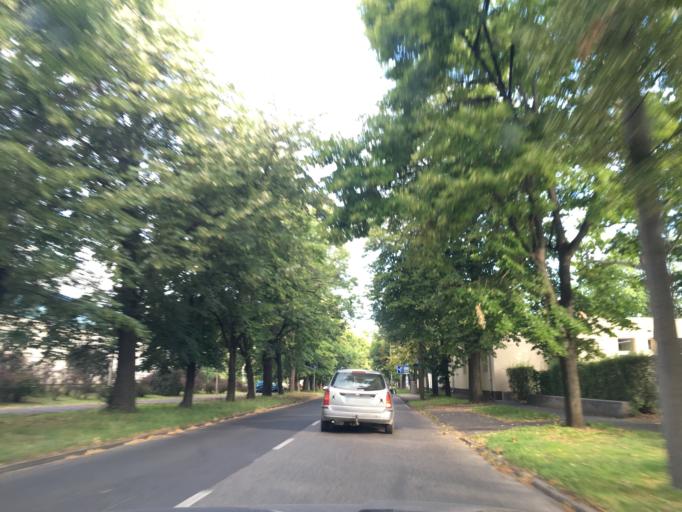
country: HU
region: Hajdu-Bihar
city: Debrecen
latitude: 47.5467
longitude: 21.6444
